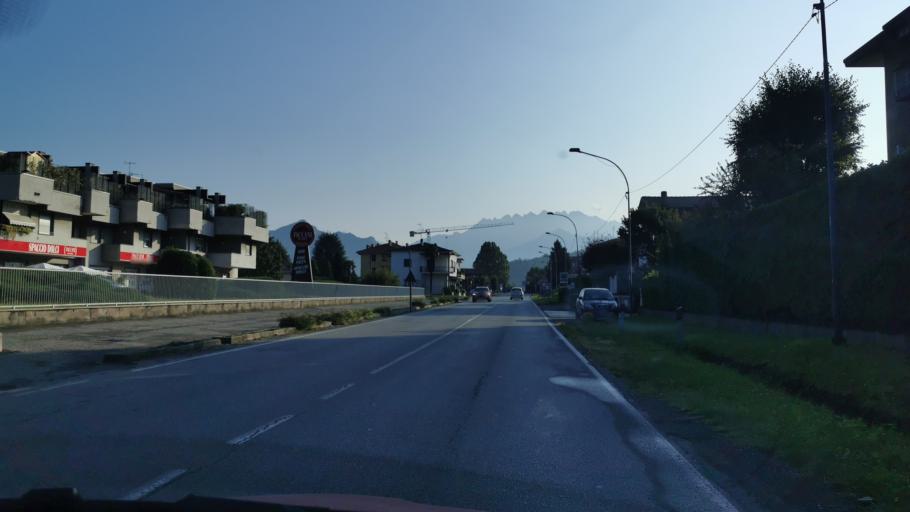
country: IT
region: Lombardy
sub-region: Provincia di Lecco
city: Oggiono
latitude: 45.7827
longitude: 9.3392
